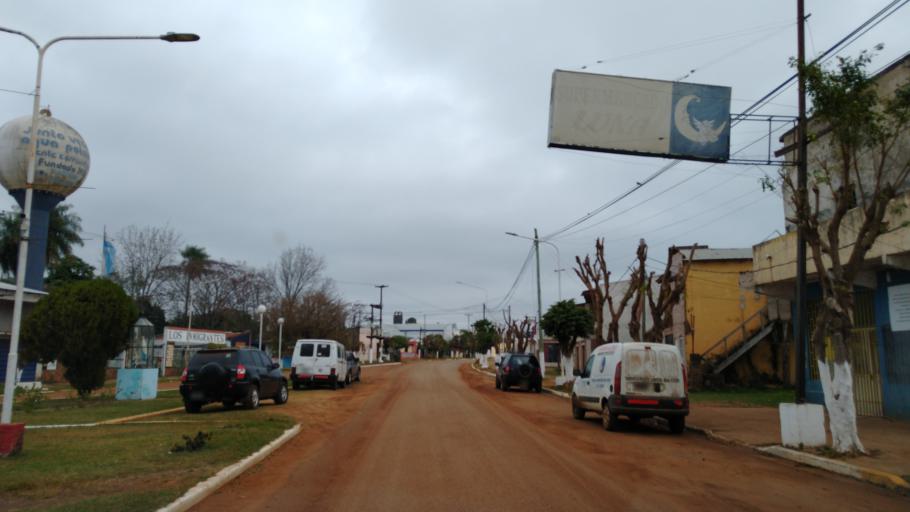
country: AR
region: Corrientes
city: Alvear
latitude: -29.0887
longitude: -56.5470
